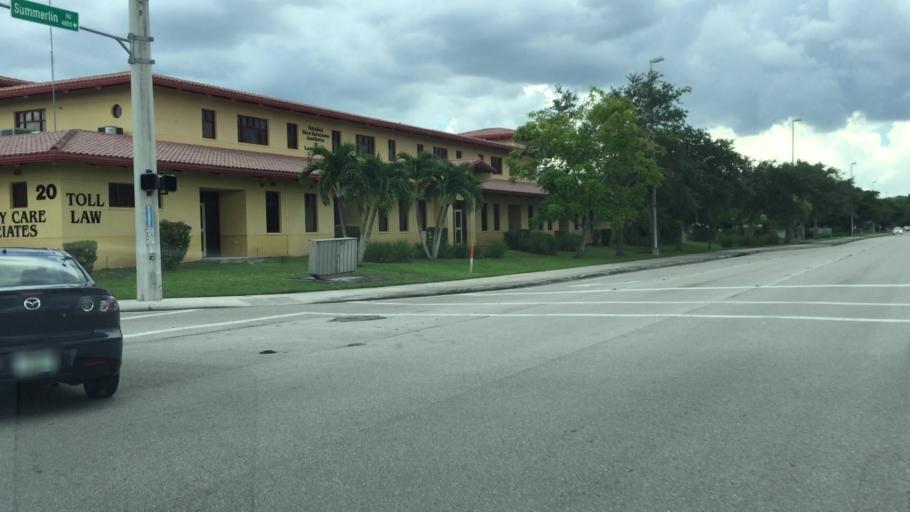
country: US
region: Florida
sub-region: Lee County
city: Pine Manor
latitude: 26.5896
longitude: -81.8836
